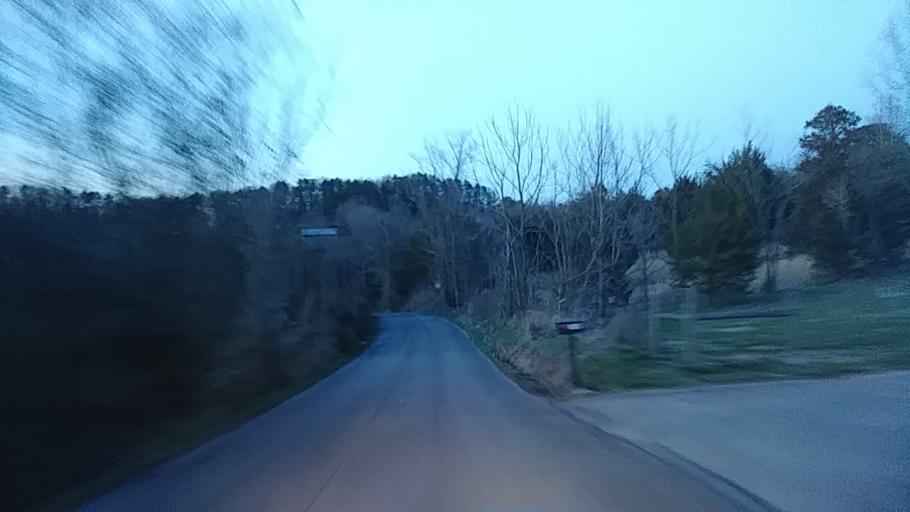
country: US
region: Tennessee
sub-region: Greene County
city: Mosheim
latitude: 36.0705
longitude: -82.9879
